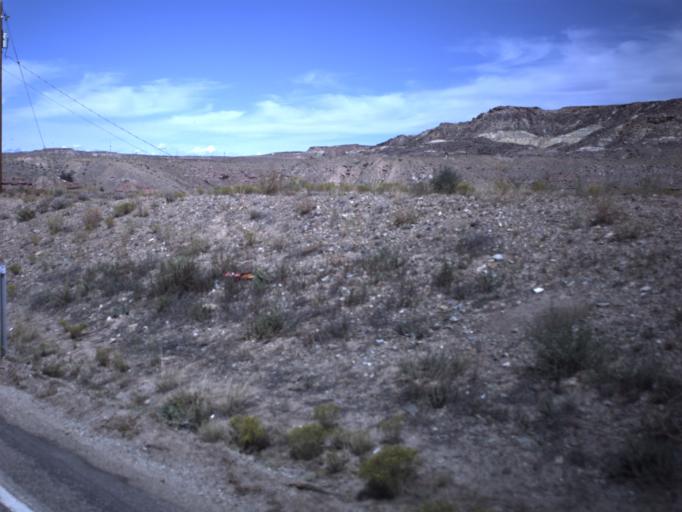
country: US
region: Colorado
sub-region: Montezuma County
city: Towaoc
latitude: 37.2168
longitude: -109.1882
